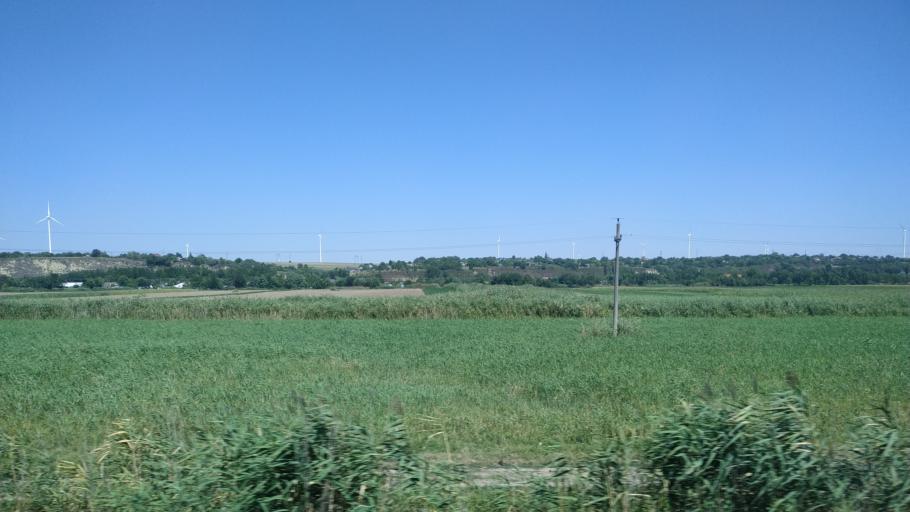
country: RO
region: Constanta
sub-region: Comuna Saligny
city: Faclia
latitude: 44.2730
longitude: 28.1015
